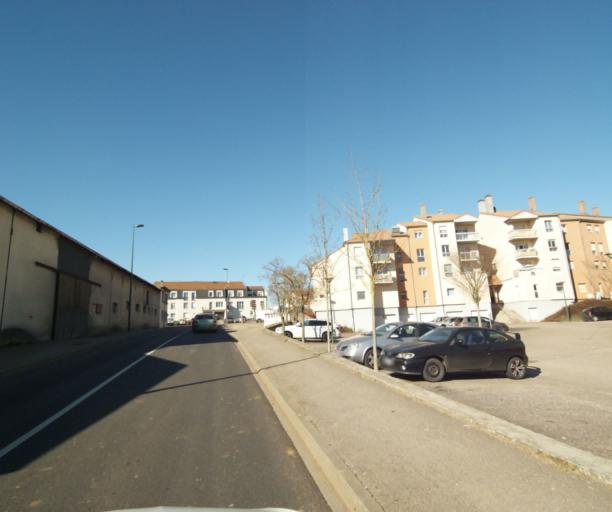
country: FR
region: Lorraine
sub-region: Departement de Meurthe-et-Moselle
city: Saulxures-les-Nancy
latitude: 48.6868
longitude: 6.2451
